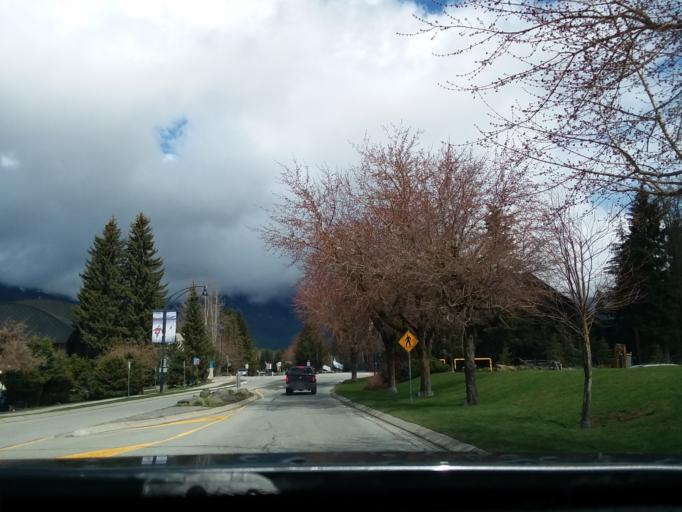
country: CA
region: British Columbia
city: Whistler
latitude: 50.1169
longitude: -122.9536
